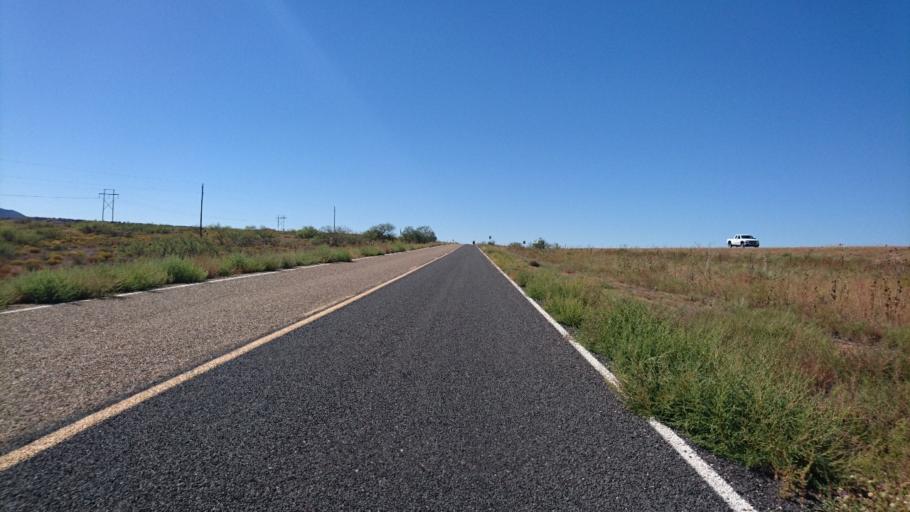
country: US
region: New Mexico
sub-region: Quay County
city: Tucumcari
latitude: 35.0824
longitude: -104.1130
